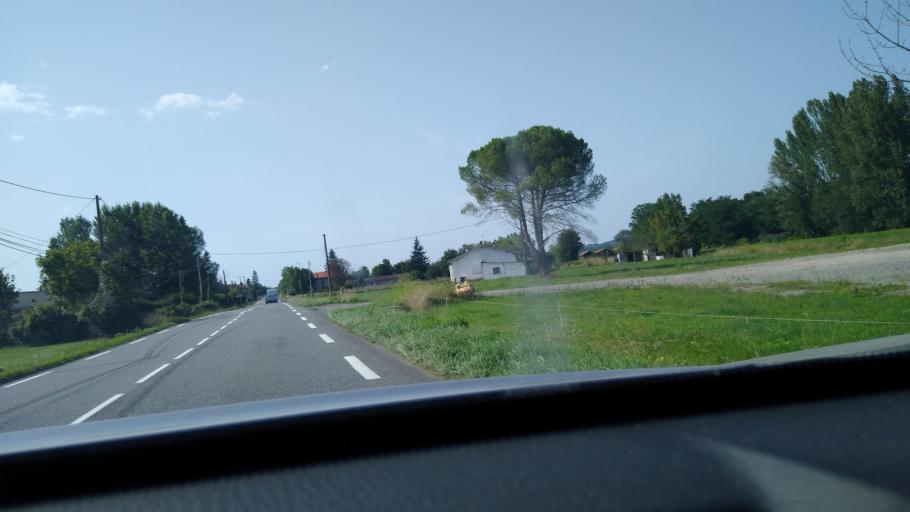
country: FR
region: Midi-Pyrenees
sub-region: Departement de la Haute-Garonne
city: Salies-du-Salat
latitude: 43.0513
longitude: 0.9829
